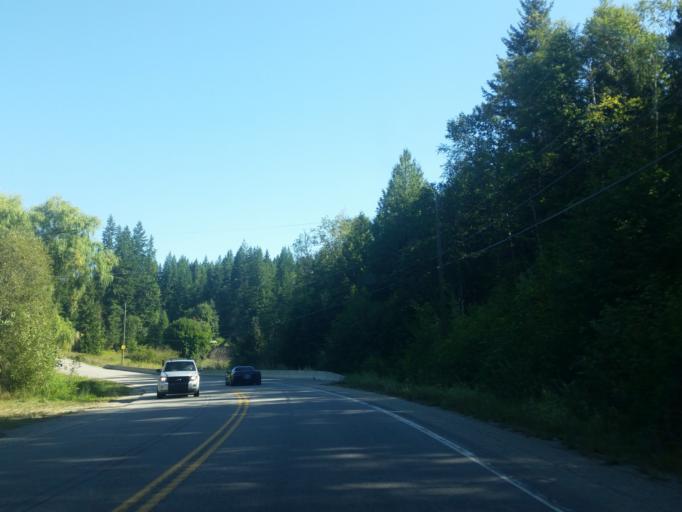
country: CA
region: British Columbia
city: Sicamous
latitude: 50.7176
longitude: -119.0323
